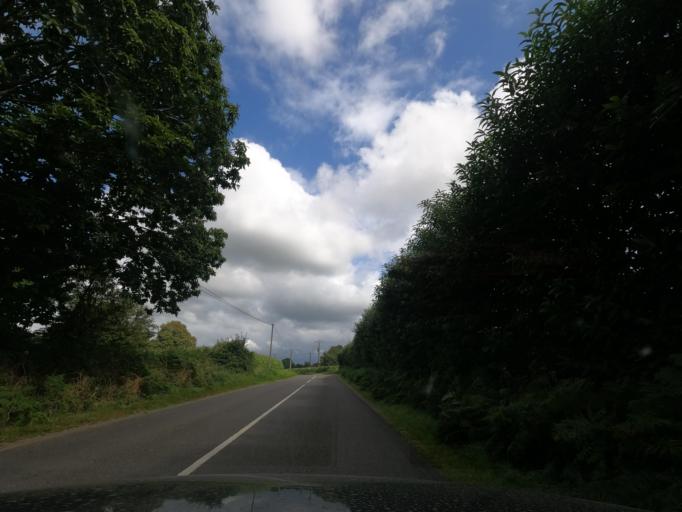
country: FR
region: Lower Normandy
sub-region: Departement de l'Orne
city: La Ferriere-aux-Etangs
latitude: 48.6691
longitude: -0.5042
